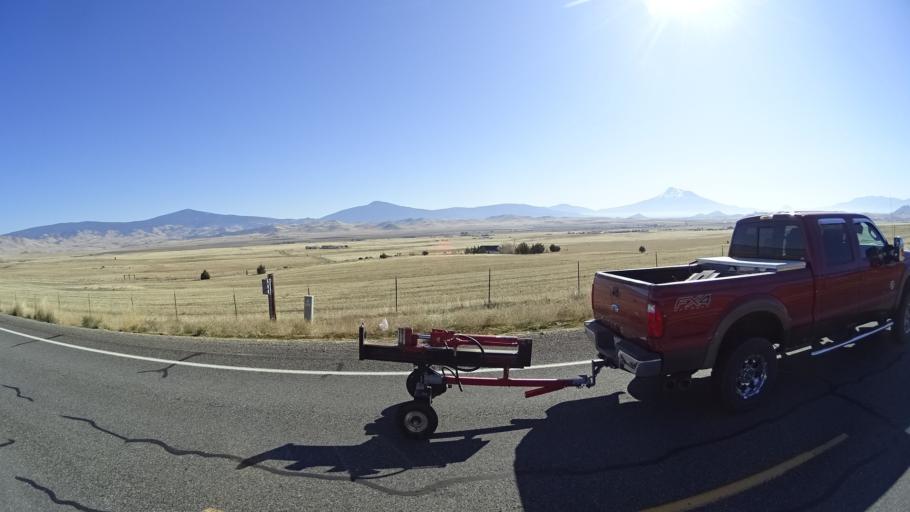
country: US
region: California
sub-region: Siskiyou County
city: Montague
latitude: 41.7981
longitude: -122.5101
